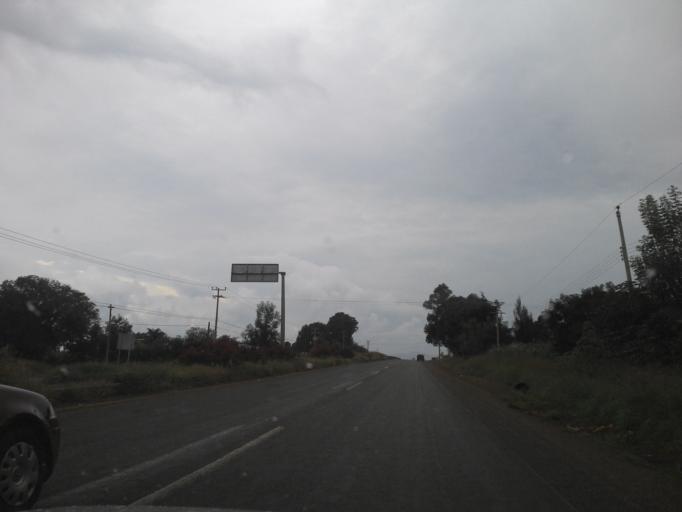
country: MX
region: Jalisco
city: Arandas
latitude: 20.7179
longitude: -102.4399
